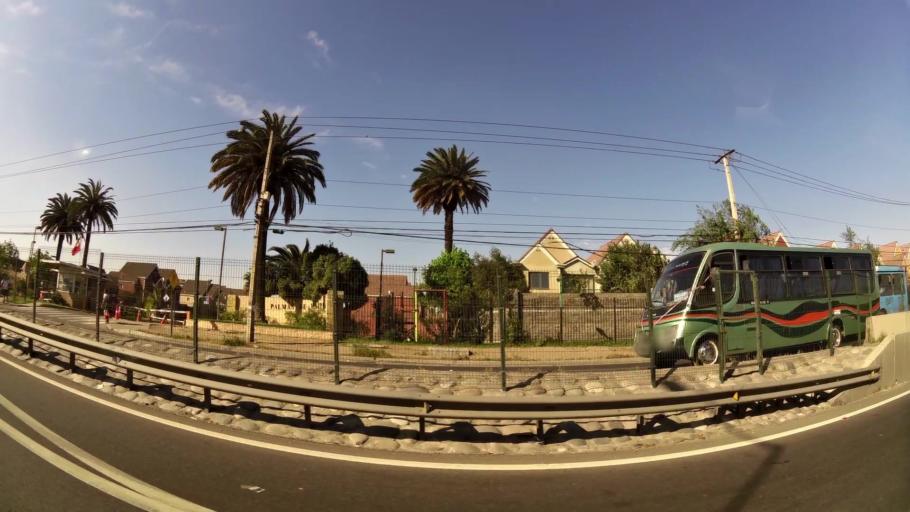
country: CL
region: Santiago Metropolitan
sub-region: Provincia de Santiago
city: Lo Prado
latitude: -33.4775
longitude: -70.7564
